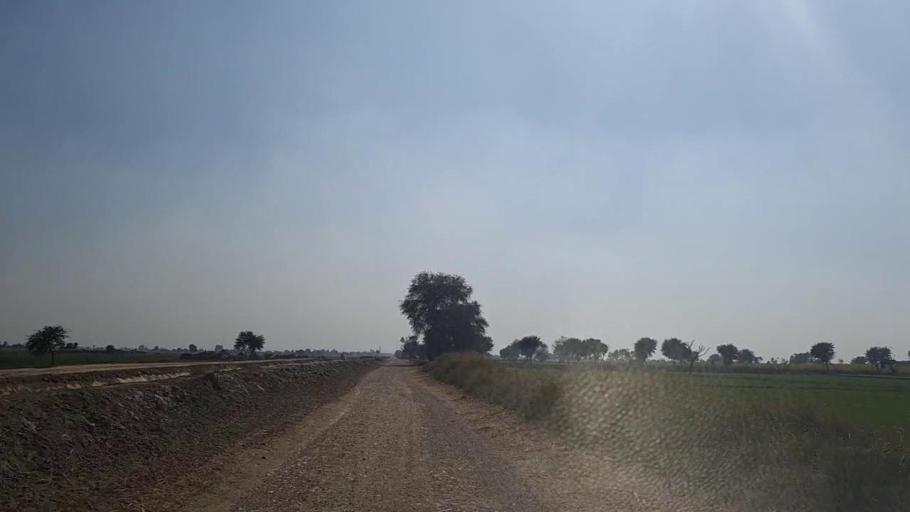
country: PK
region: Sindh
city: Shahpur Chakar
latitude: 26.2045
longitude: 68.5837
